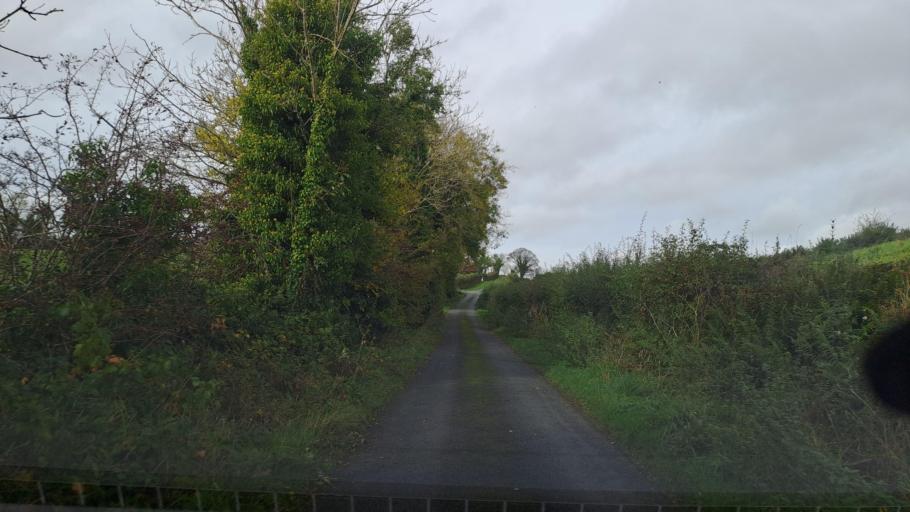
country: IE
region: Ulster
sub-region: County Monaghan
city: Carrickmacross
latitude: 54.0040
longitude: -6.7842
